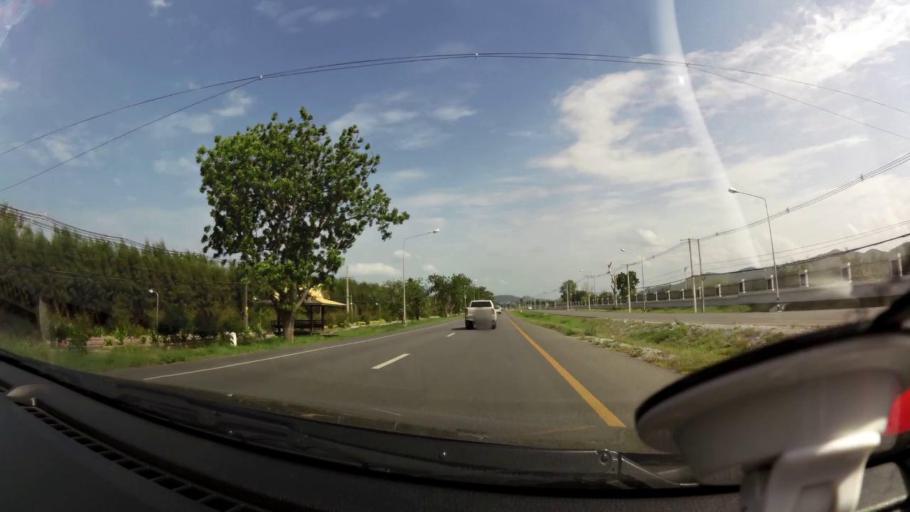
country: TH
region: Prachuap Khiri Khan
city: Hua Hin
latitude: 12.5075
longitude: 99.9675
